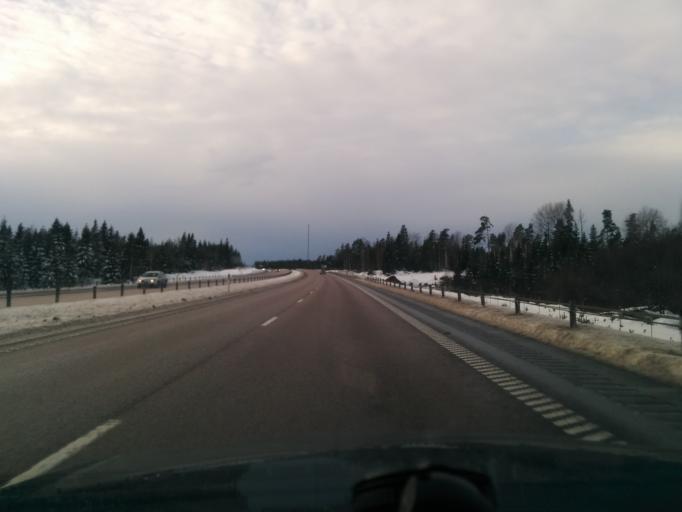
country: SE
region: Uppsala
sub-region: Enkopings Kommun
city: Hummelsta
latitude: 59.6408
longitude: 16.9054
